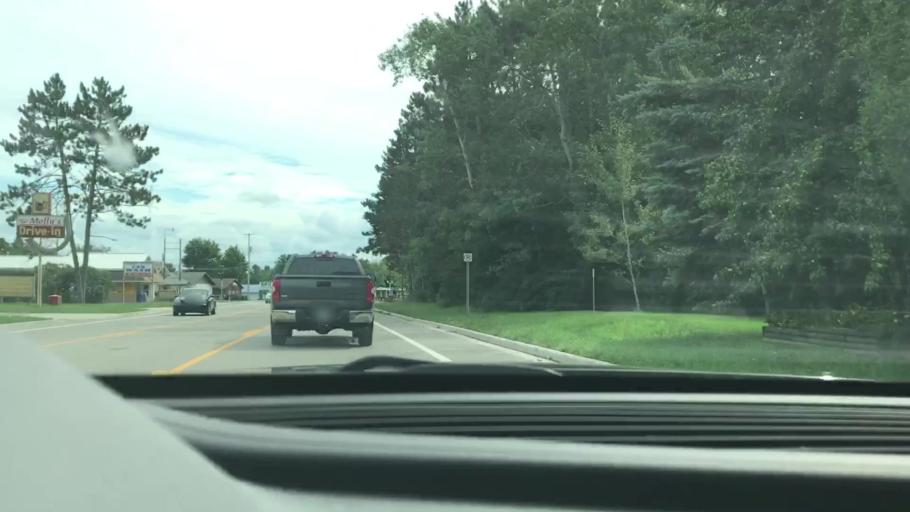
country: US
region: Michigan
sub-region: Missaukee County
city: Lake City
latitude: 44.3212
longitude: -85.2118
